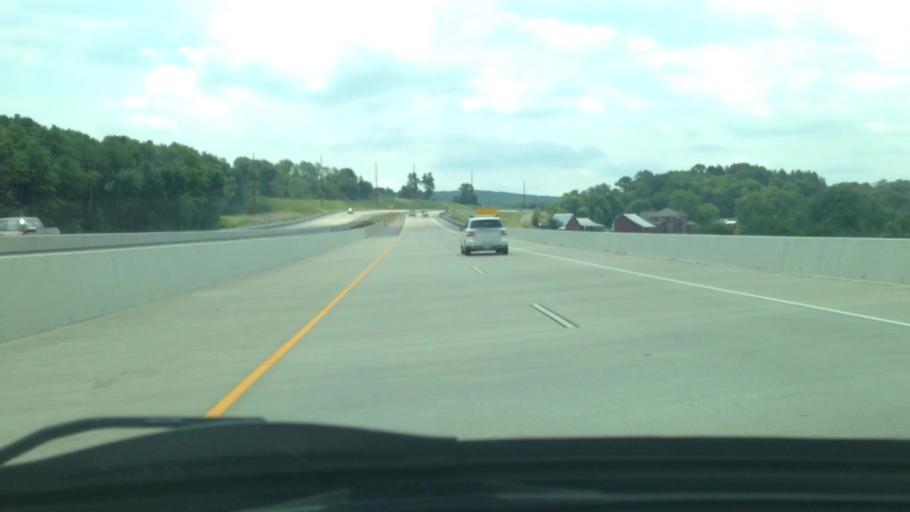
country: US
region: Wisconsin
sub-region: Sauk County
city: West Baraboo
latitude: 43.4329
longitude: -89.7766
